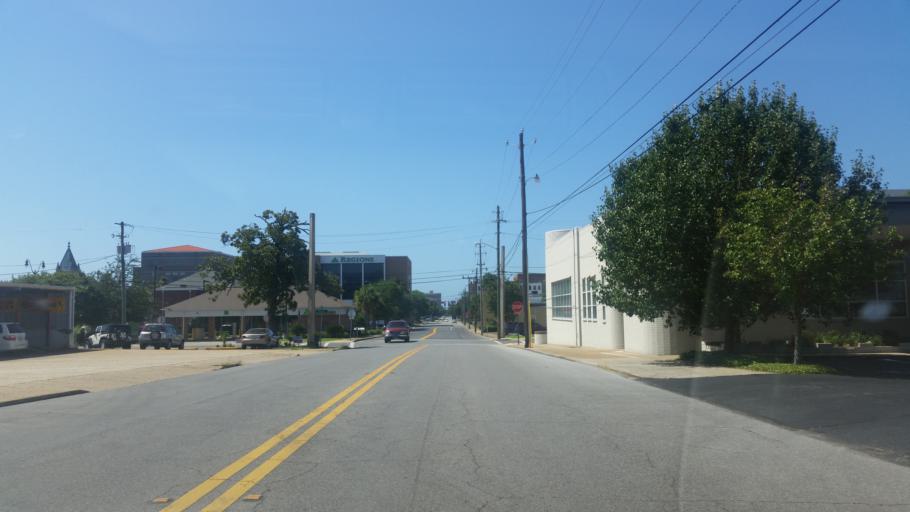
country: US
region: Florida
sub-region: Escambia County
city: Pensacola
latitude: 30.4158
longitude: -87.2176
